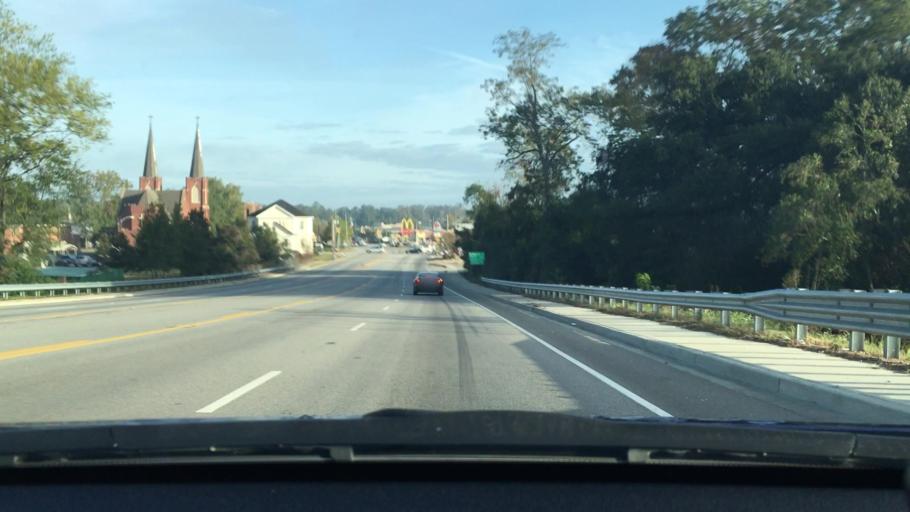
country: US
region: South Carolina
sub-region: Sumter County
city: Sumter
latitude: 33.9182
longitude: -80.3360
